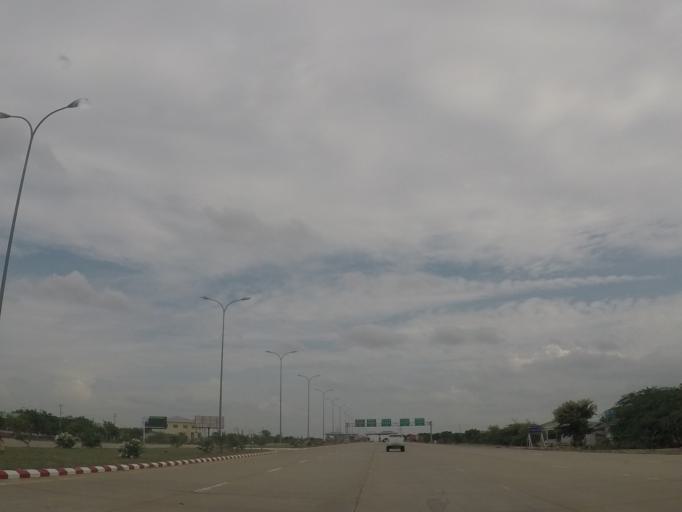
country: MM
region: Sagain
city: Sagaing
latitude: 21.7578
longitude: 95.9752
